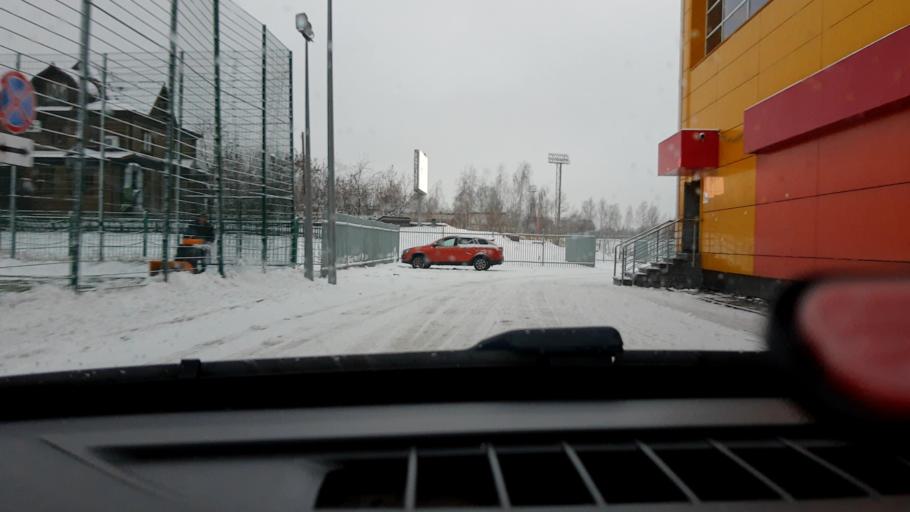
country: RU
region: Nizjnij Novgorod
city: Neklyudovo
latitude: 56.3425
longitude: 43.8593
